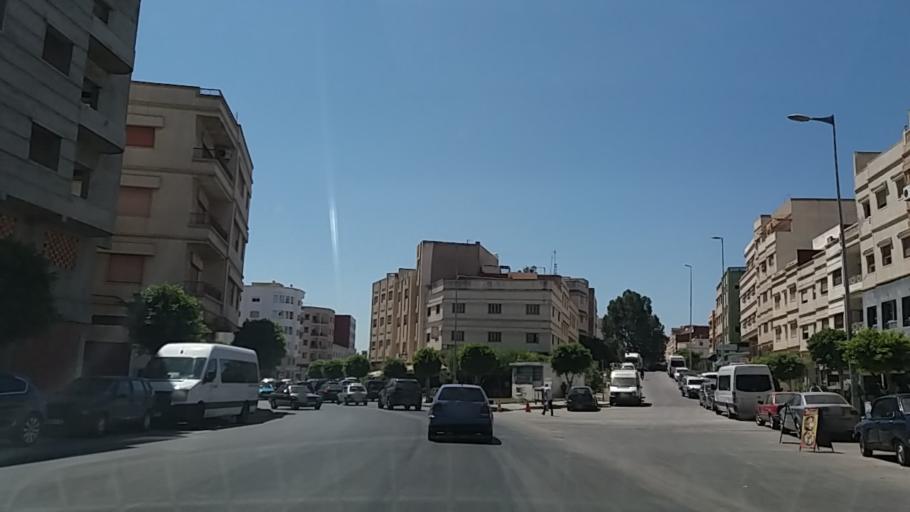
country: MA
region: Tanger-Tetouan
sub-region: Tanger-Assilah
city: Tangier
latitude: 35.7564
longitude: -5.8014
